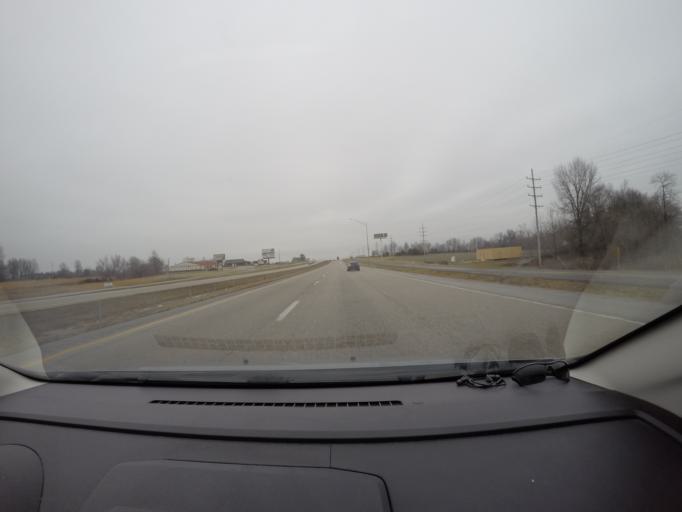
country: US
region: Missouri
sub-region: Montgomery County
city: Montgomery City
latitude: 38.8980
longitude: -91.4513
